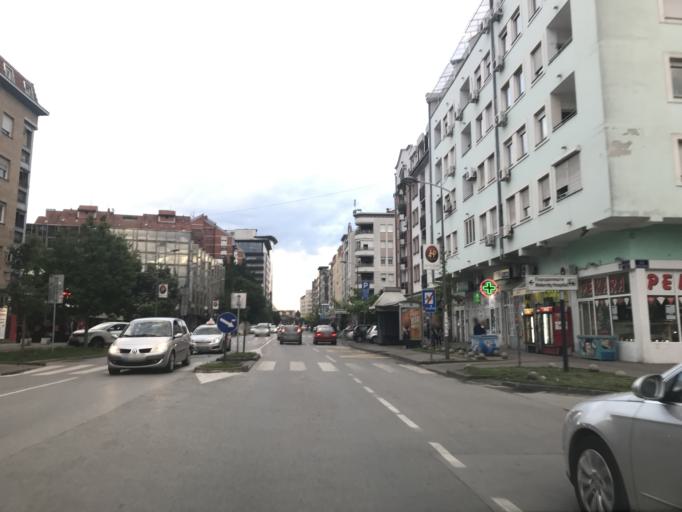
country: RS
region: Autonomna Pokrajina Vojvodina
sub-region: Juznobacki Okrug
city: Novi Sad
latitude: 45.2547
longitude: 19.8304
